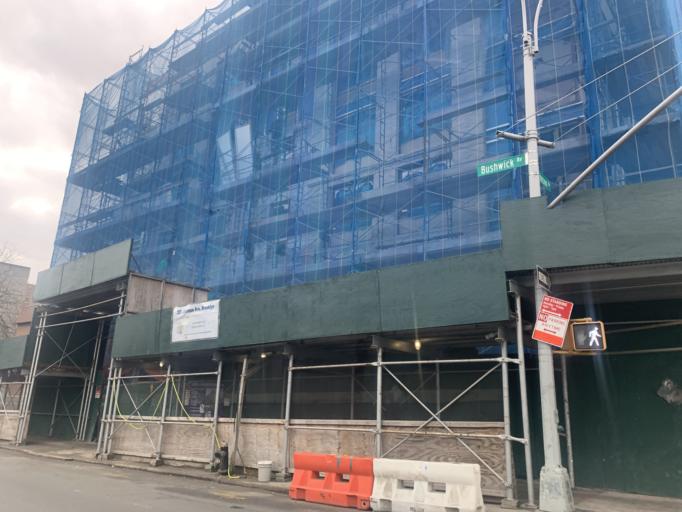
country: US
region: New York
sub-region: Queens County
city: Long Island City
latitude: 40.7069
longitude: -73.9397
